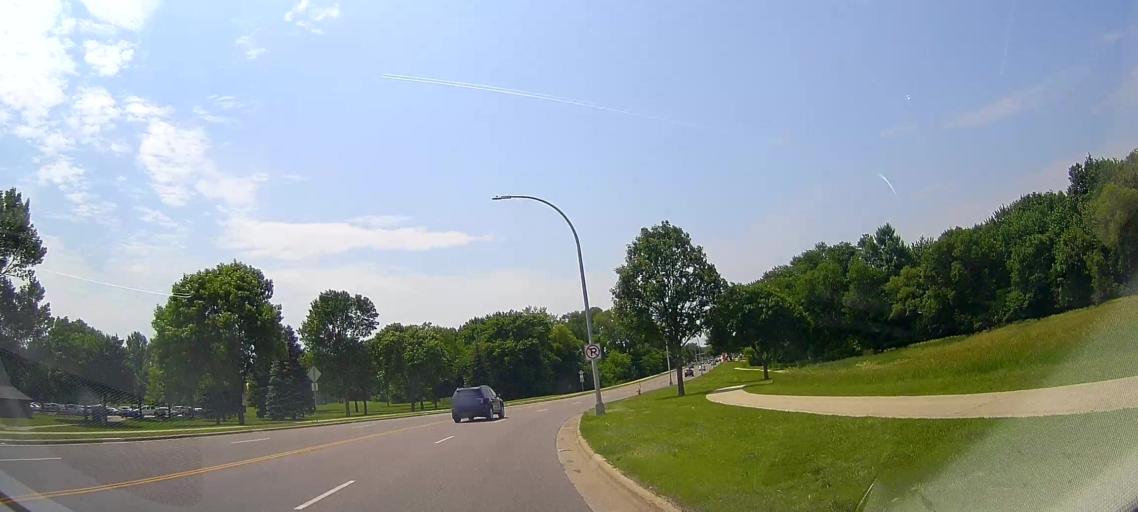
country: US
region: South Dakota
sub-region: Minnehaha County
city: Sioux Falls
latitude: 43.5078
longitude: -96.7608
